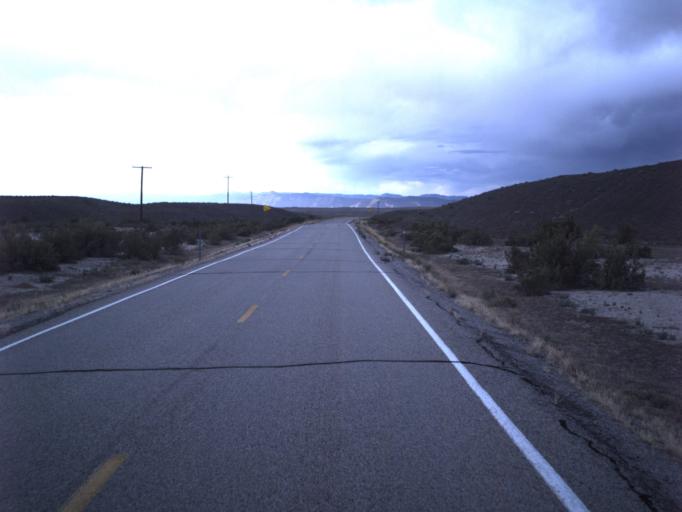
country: US
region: Utah
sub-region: Grand County
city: Moab
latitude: 38.8787
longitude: -109.3092
